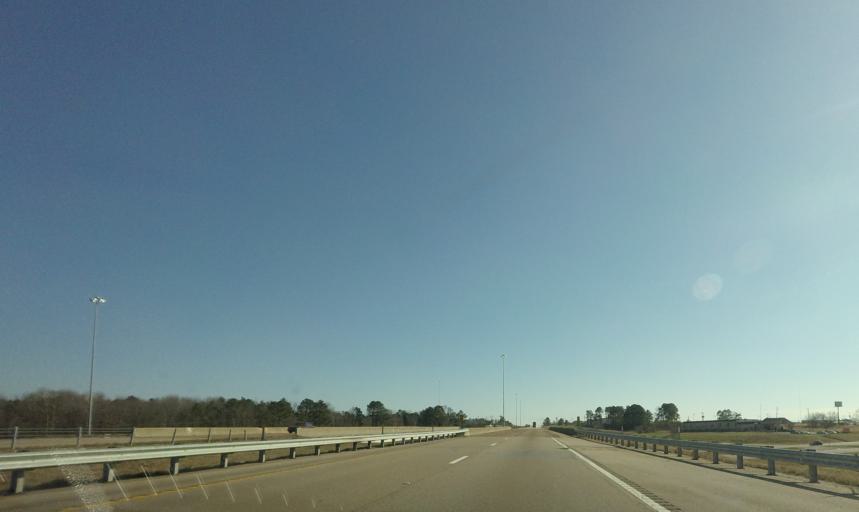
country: US
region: Mississippi
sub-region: Marshall County
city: Holly Springs
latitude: 34.7481
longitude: -89.4554
